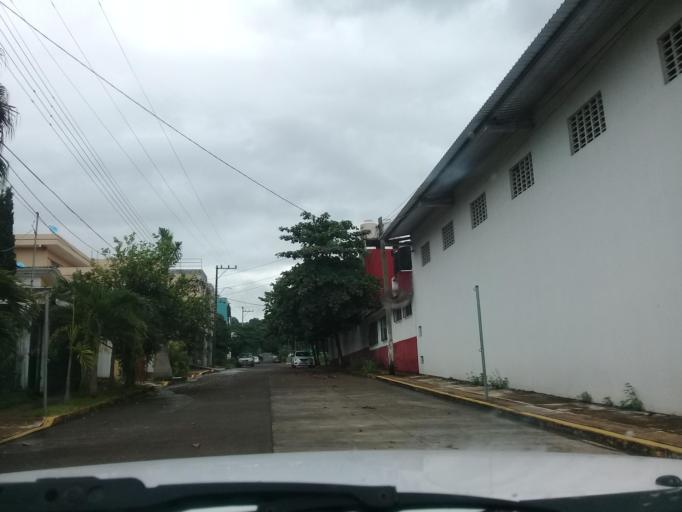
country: MX
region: Veracruz
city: San Andres Tuxtla
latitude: 18.4350
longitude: -95.1919
